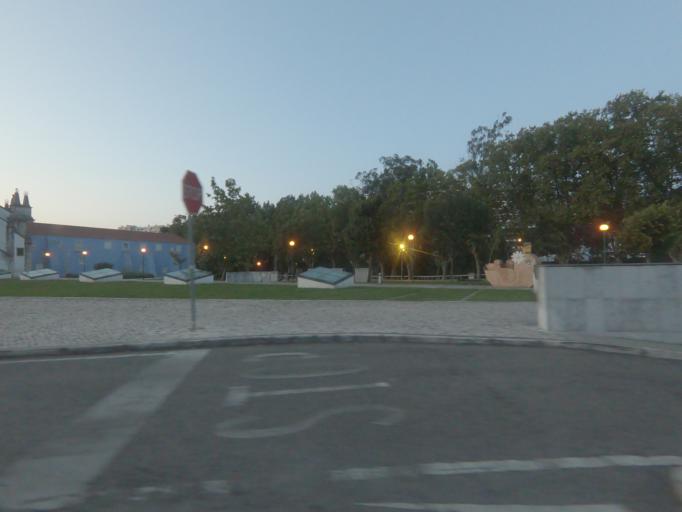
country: PT
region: Leiria
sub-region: Leiria
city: Leiria
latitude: 39.7406
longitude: -8.8018
